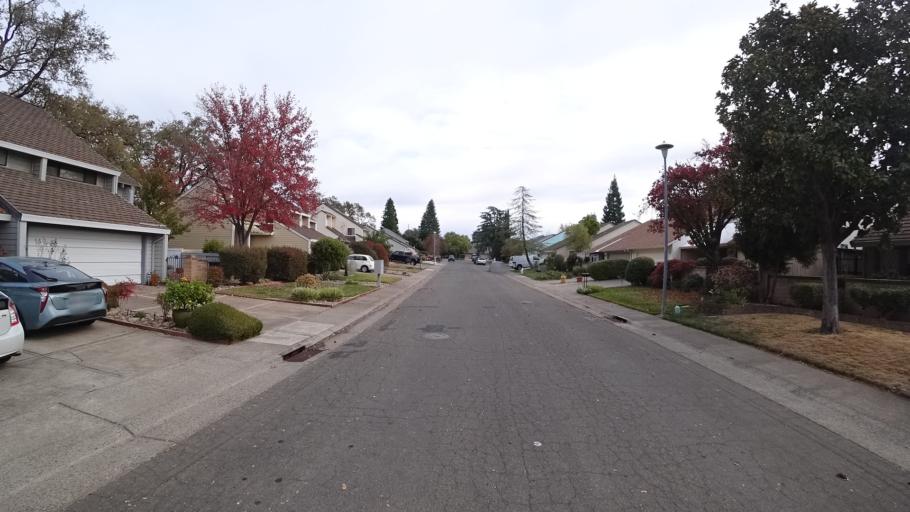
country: US
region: California
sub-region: Sacramento County
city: Fair Oaks
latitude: 38.6709
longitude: -121.2668
